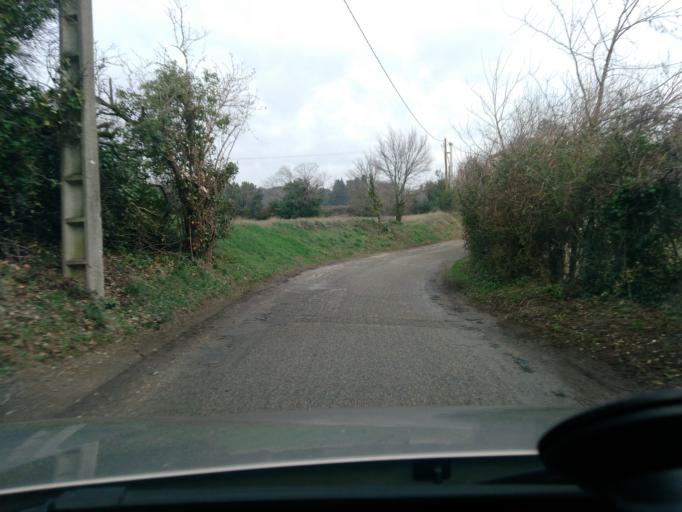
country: FR
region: Rhone-Alpes
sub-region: Departement de la Drome
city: Montelimar
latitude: 44.5539
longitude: 4.7709
